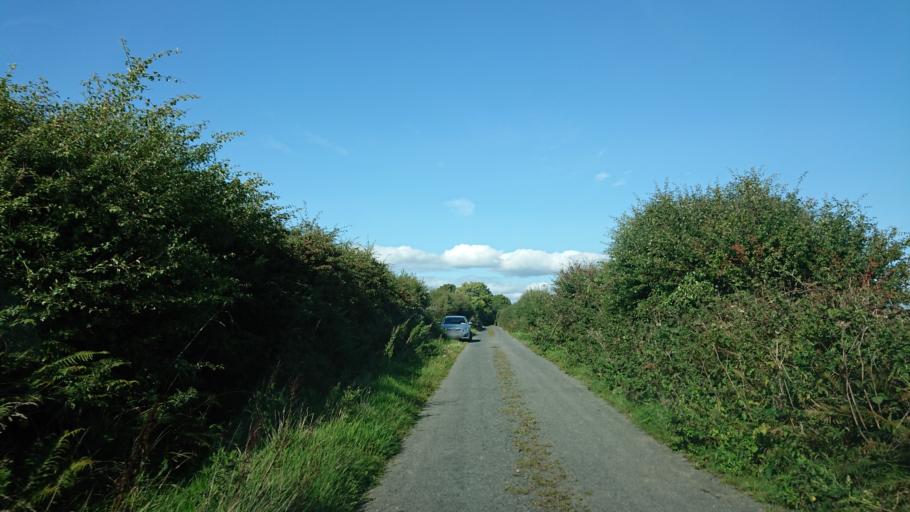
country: IE
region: Munster
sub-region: Waterford
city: Waterford
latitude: 52.2079
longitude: -7.0562
